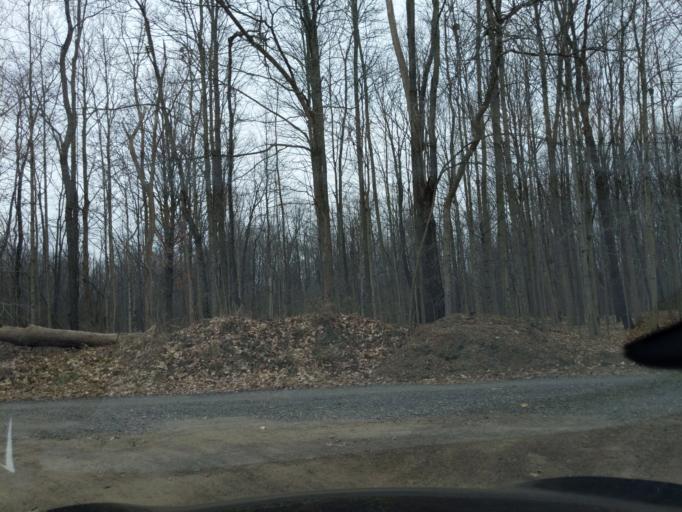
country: US
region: Michigan
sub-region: Eaton County
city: Potterville
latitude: 42.6186
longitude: -84.7552
